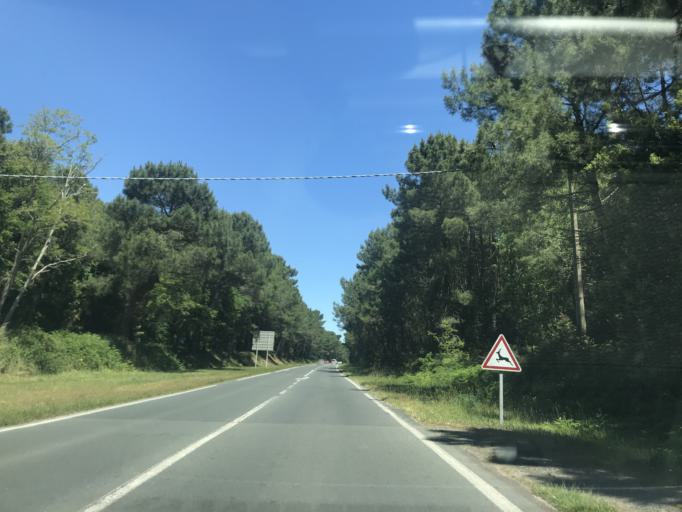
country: FR
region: Poitou-Charentes
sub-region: Departement de la Charente-Maritime
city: Saint-Palais-sur-Mer
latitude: 45.6581
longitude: -1.0872
